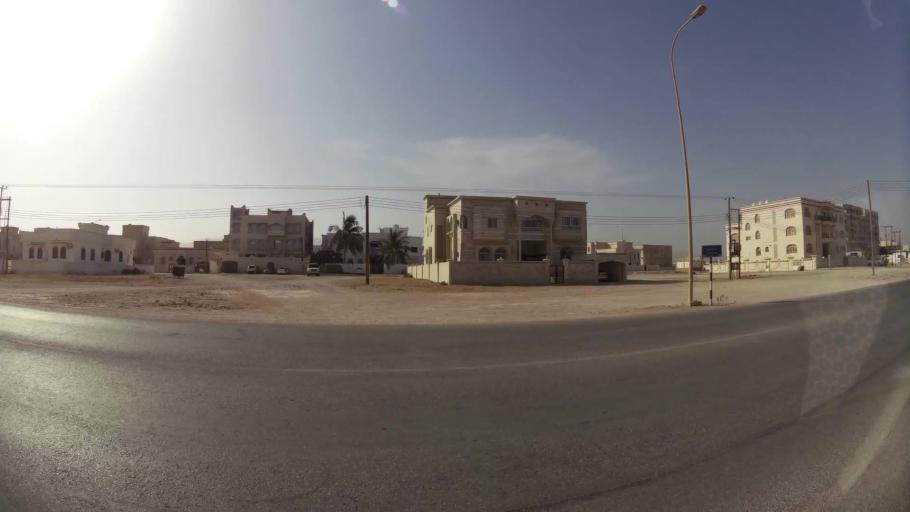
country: OM
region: Zufar
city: Salalah
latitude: 17.0068
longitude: 54.0189
